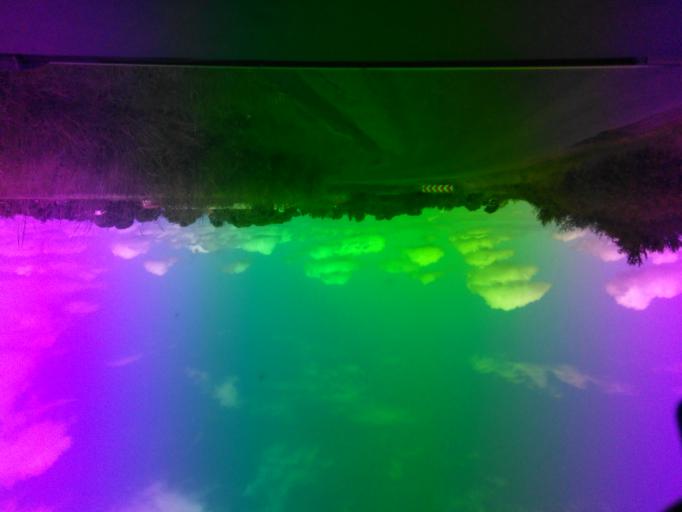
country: DK
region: Zealand
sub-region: Kalundborg Kommune
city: Svebolle
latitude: 55.5934
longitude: 11.3127
